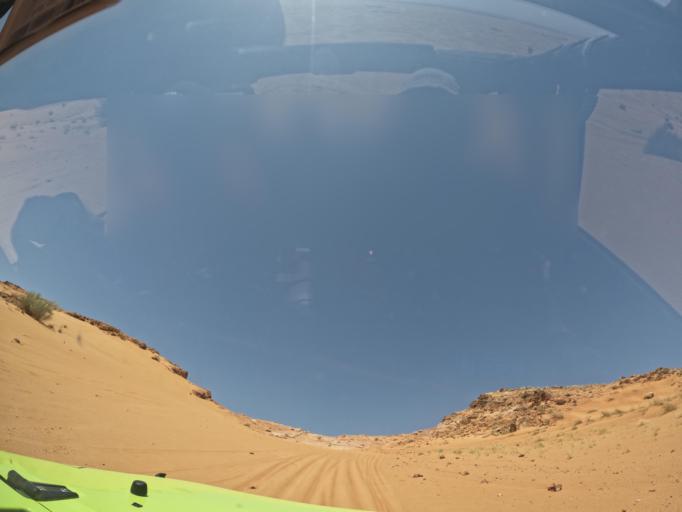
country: AE
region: Ash Shariqah
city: Adh Dhayd
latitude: 25.0197
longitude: 55.7277
